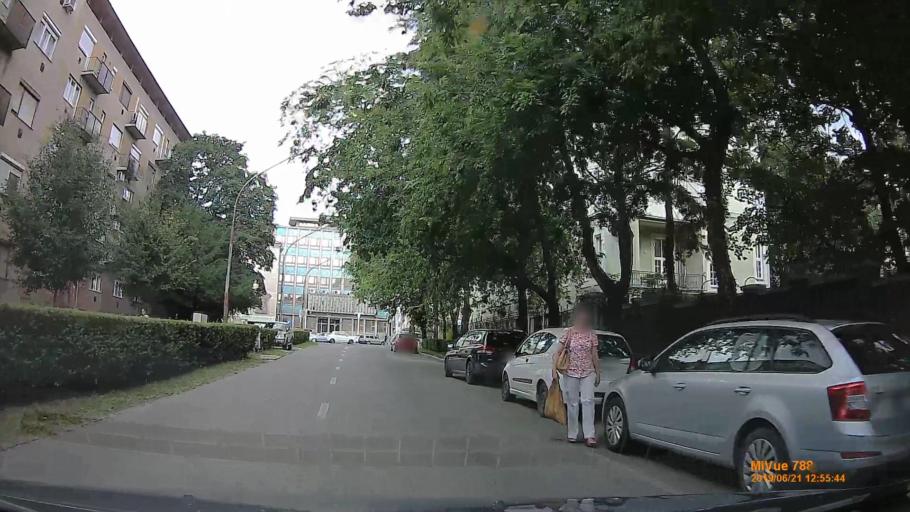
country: HU
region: Baranya
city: Pecs
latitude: 46.0738
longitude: 18.2362
